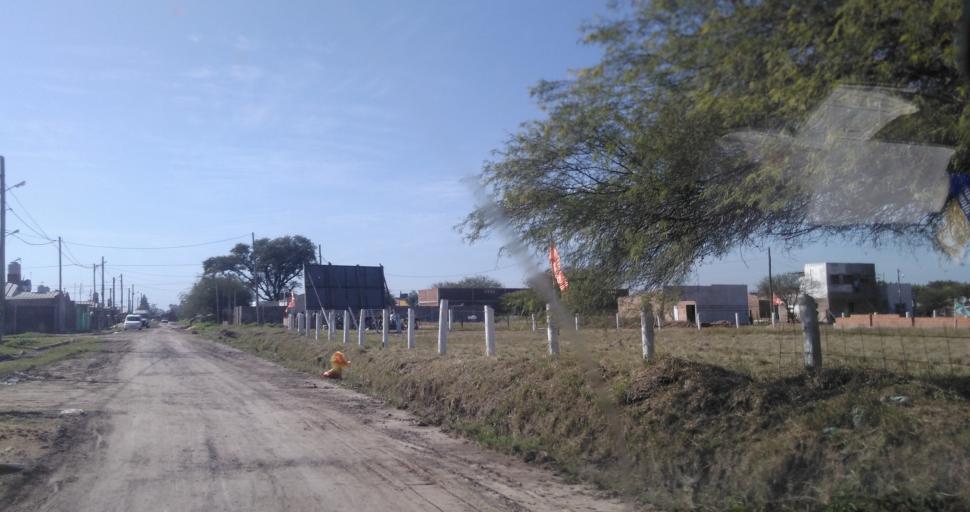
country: AR
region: Chaco
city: Fontana
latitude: -27.4583
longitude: -59.0493
